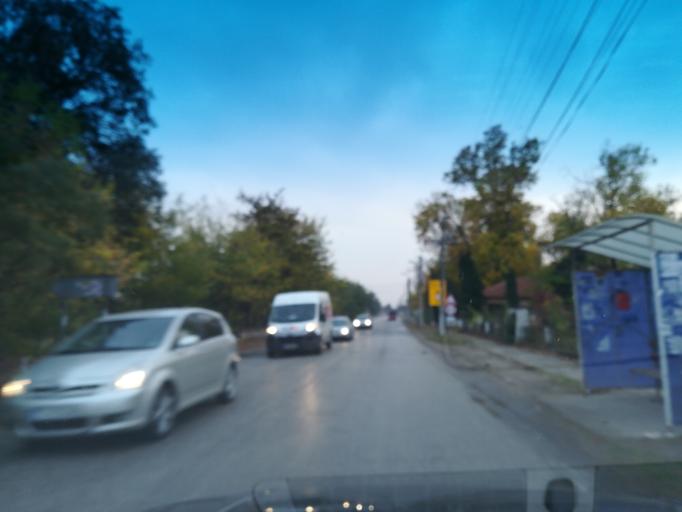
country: BG
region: Stara Zagora
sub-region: Obshtina Chirpan
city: Chirpan
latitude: 42.1767
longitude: 25.2094
